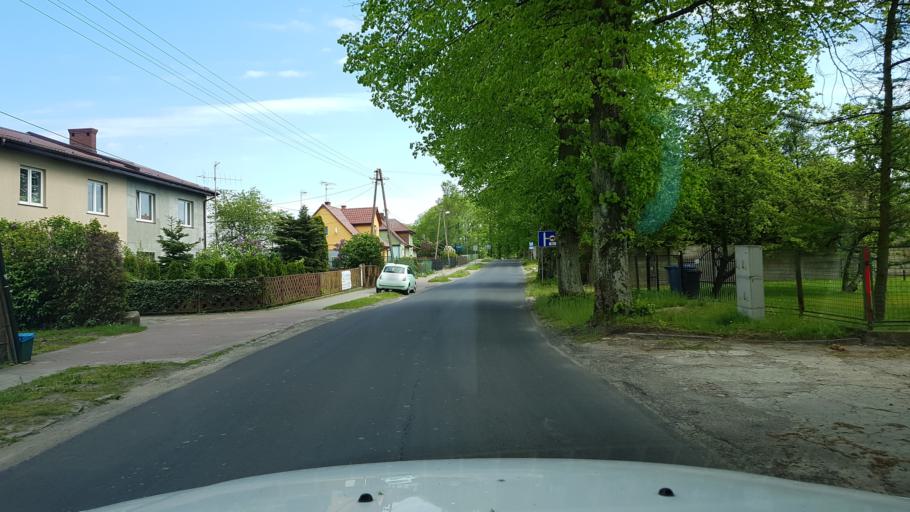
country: PL
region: West Pomeranian Voivodeship
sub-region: Powiat koszalinski
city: Mielno
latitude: 54.2497
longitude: 16.0186
